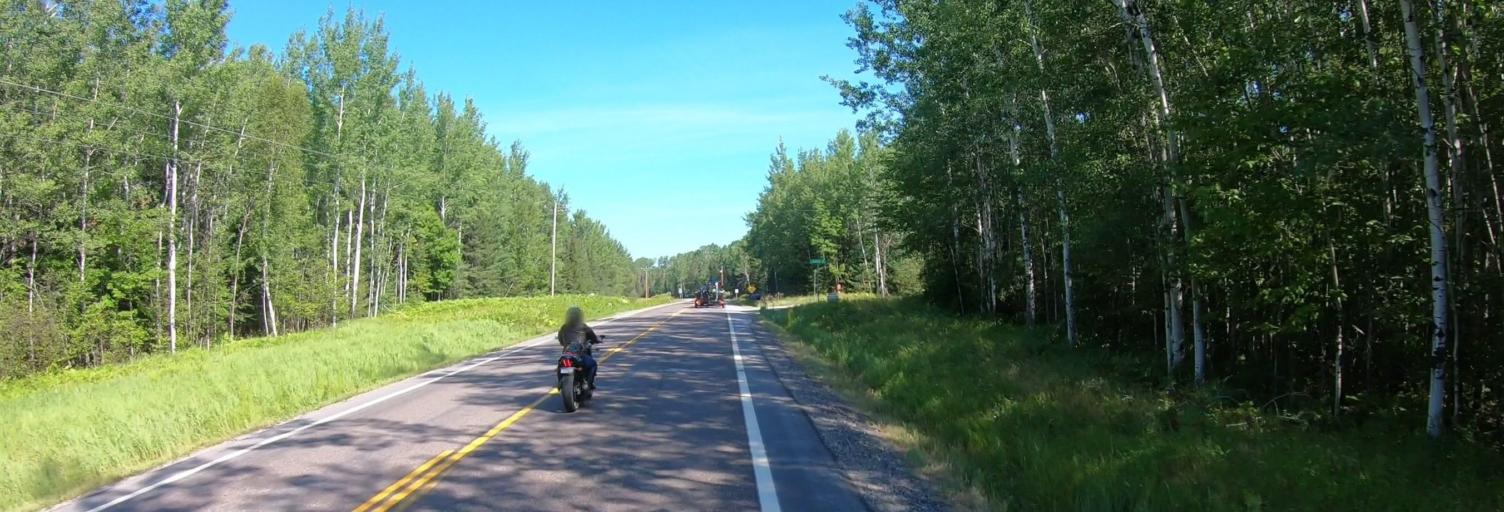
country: US
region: Minnesota
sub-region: Saint Louis County
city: Mountain Iron
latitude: 47.9176
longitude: -92.6572
